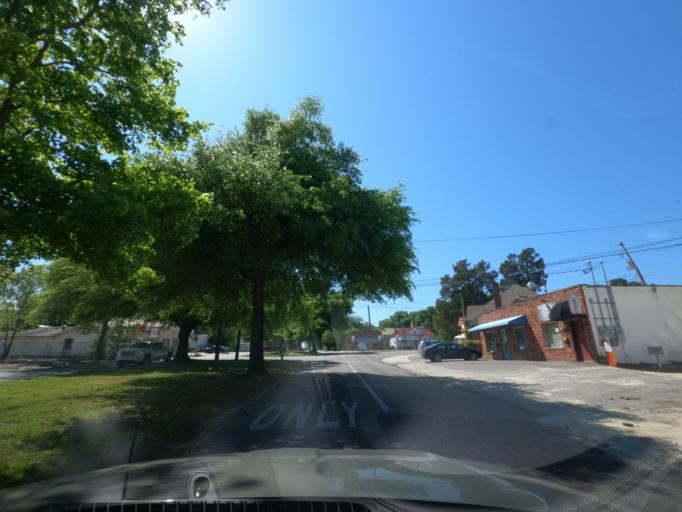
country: US
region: Georgia
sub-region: Richmond County
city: Augusta
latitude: 33.4710
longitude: -82.0272
